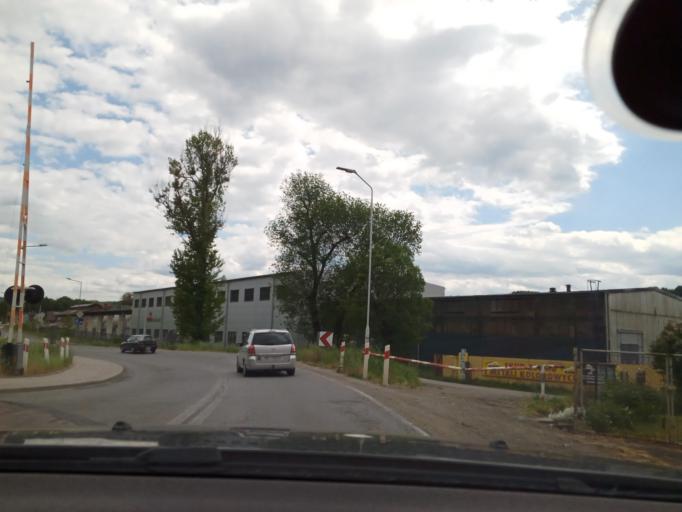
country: PL
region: Lesser Poland Voivodeship
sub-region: Powiat limanowski
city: Limanowa
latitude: 49.7277
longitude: 20.3992
